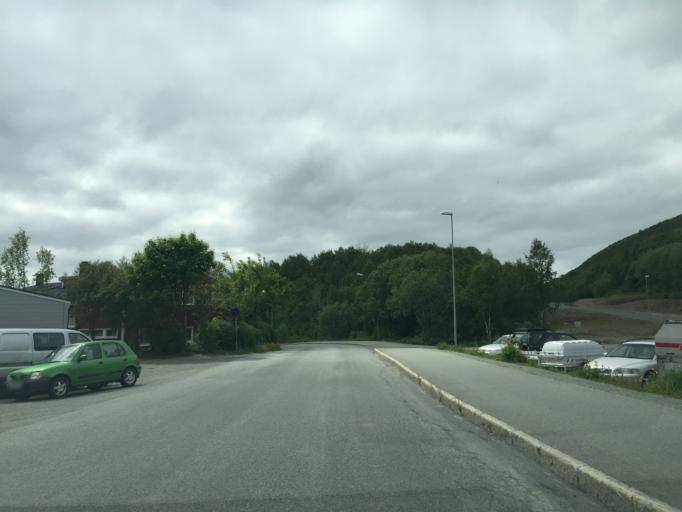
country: NO
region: Nordland
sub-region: Bodo
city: Lopsmarka
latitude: 67.2833
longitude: 14.5294
